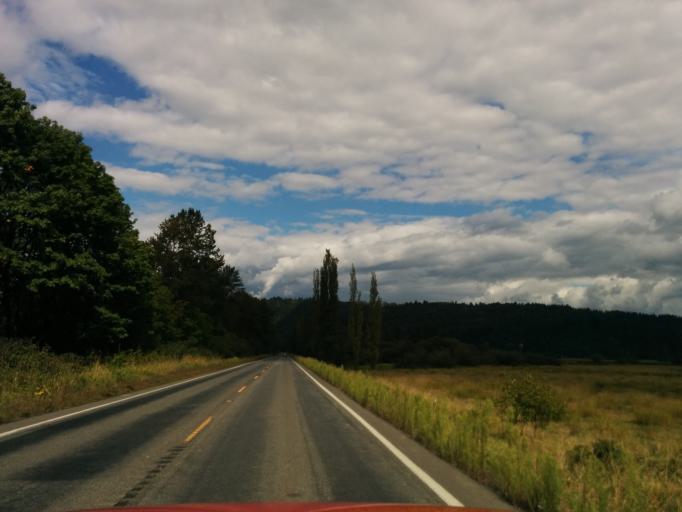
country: US
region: Washington
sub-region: King County
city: Duvall
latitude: 47.7541
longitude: -121.9797
